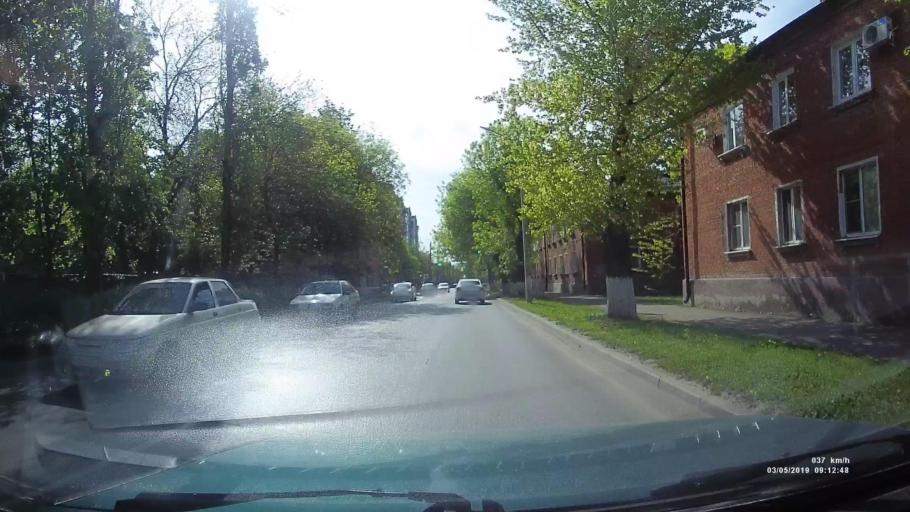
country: RU
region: Rostov
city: Azov
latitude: 47.1005
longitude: 39.4229
